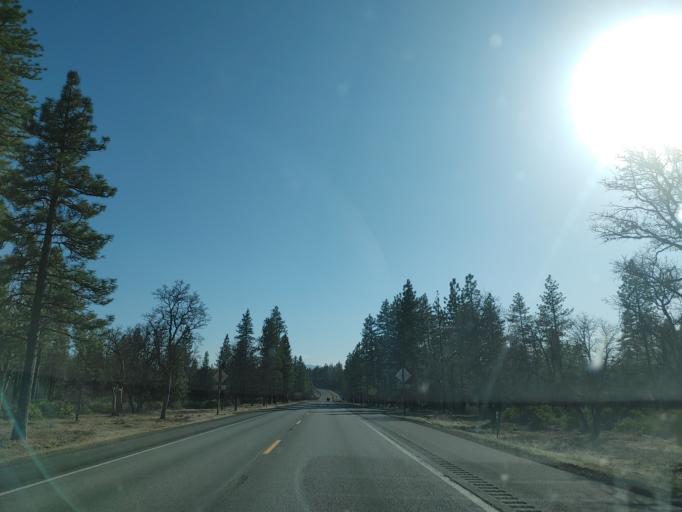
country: US
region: California
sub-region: Shasta County
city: Burney
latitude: 40.9355
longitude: -121.6098
